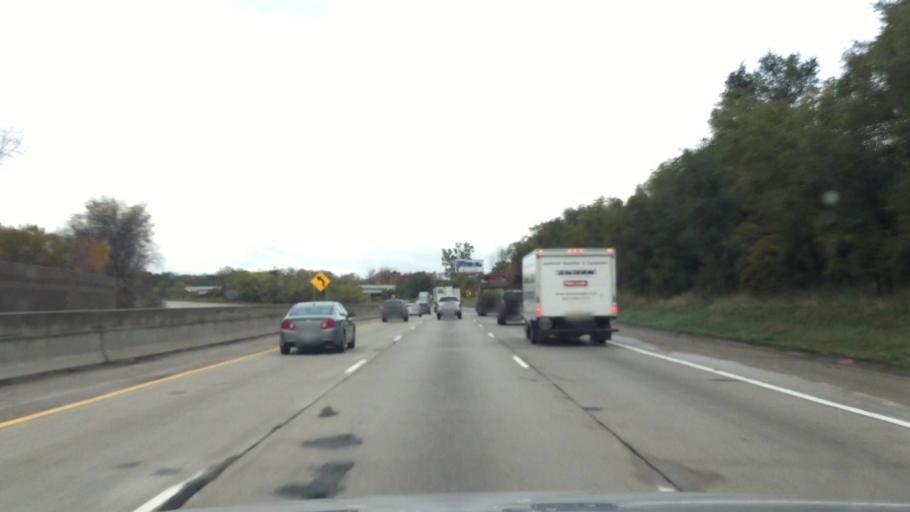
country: US
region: Michigan
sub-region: Washtenaw County
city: Ypsilanti
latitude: 42.2296
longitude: -83.5751
